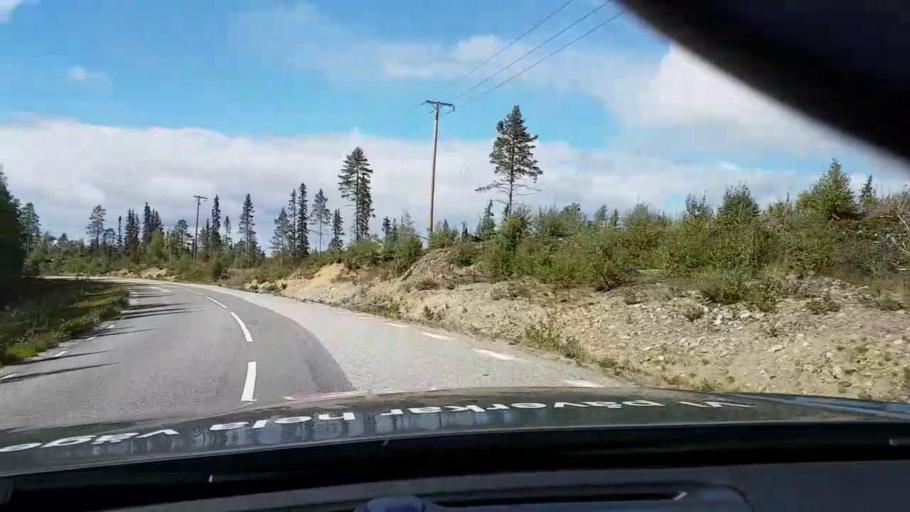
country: SE
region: Vaesterbotten
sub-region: Asele Kommun
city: Asele
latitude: 63.8276
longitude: 17.4722
